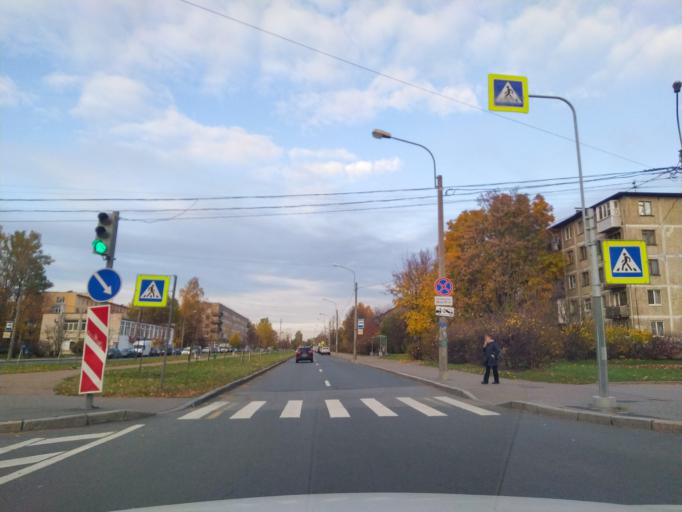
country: RU
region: Leningrad
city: Kalininskiy
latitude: 59.9713
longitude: 30.3975
